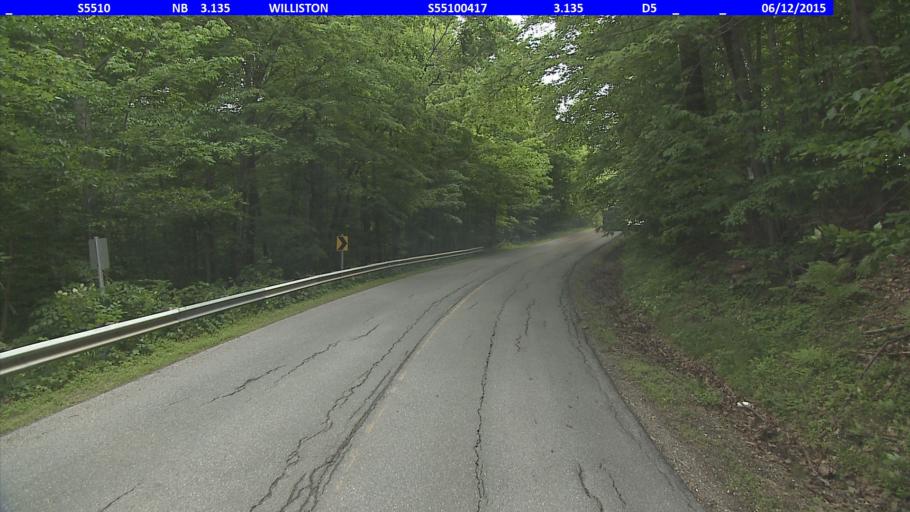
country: US
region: Vermont
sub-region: Chittenden County
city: Williston
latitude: 44.4164
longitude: -73.0858
